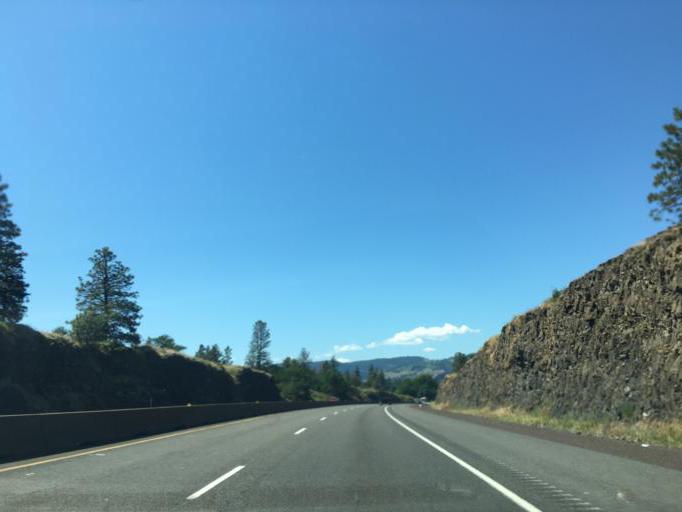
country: US
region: Washington
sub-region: Klickitat County
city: White Salmon
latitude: 45.6953
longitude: -121.3605
